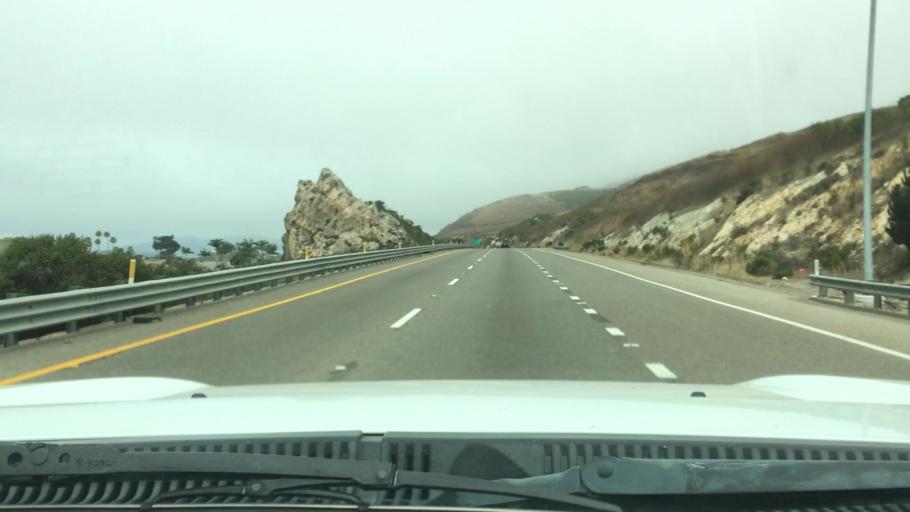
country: US
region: California
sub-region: San Luis Obispo County
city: Pismo Beach
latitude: 35.1486
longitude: -120.6468
